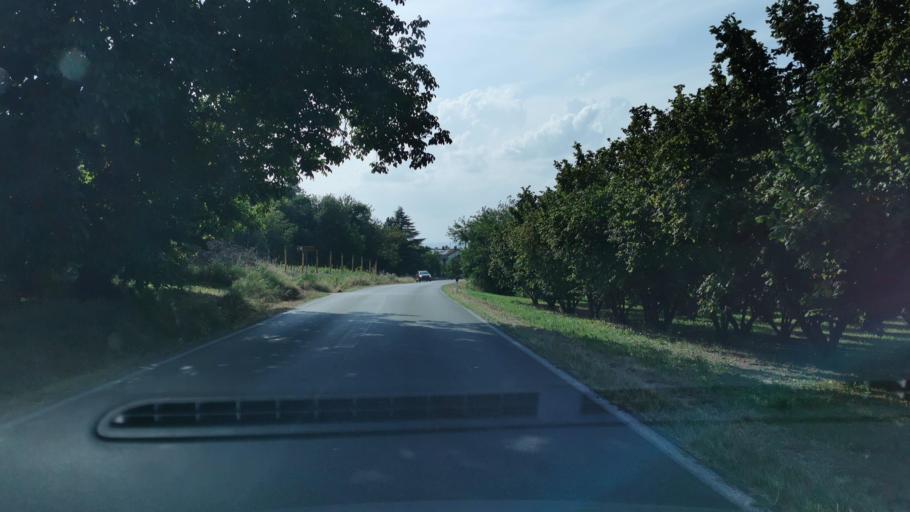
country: IT
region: Piedmont
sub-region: Provincia di Cuneo
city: La Morra
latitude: 44.6440
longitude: 7.9193
